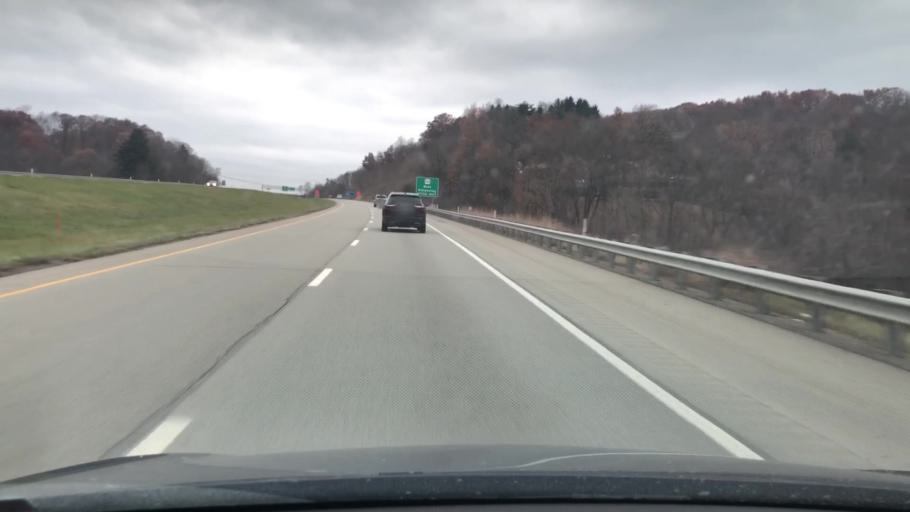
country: US
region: Pennsylvania
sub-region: Armstrong County
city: West Kittanning
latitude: 40.8064
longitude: -79.5388
